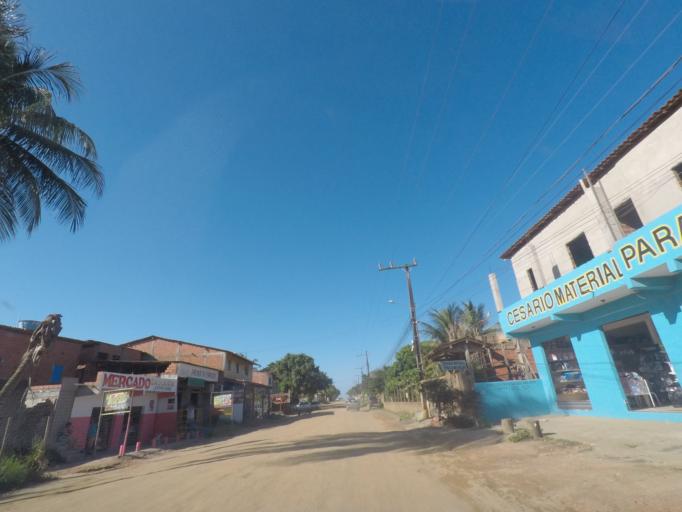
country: BR
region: Bahia
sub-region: Marau
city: Marau
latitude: -14.0412
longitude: -38.9556
